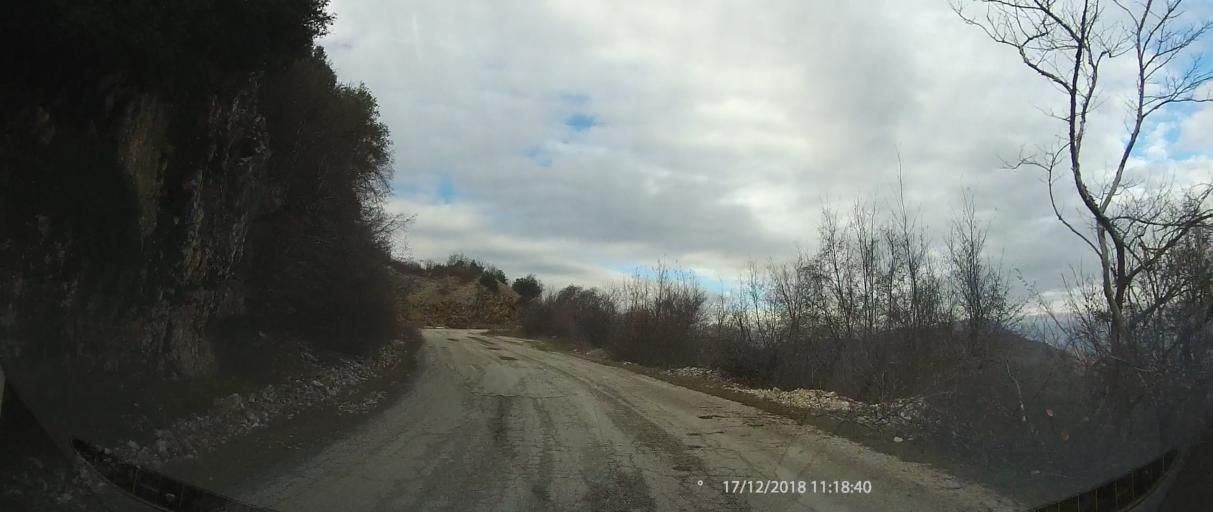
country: GR
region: Epirus
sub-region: Nomos Ioanninon
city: Kalpaki
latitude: 39.9556
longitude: 20.6568
